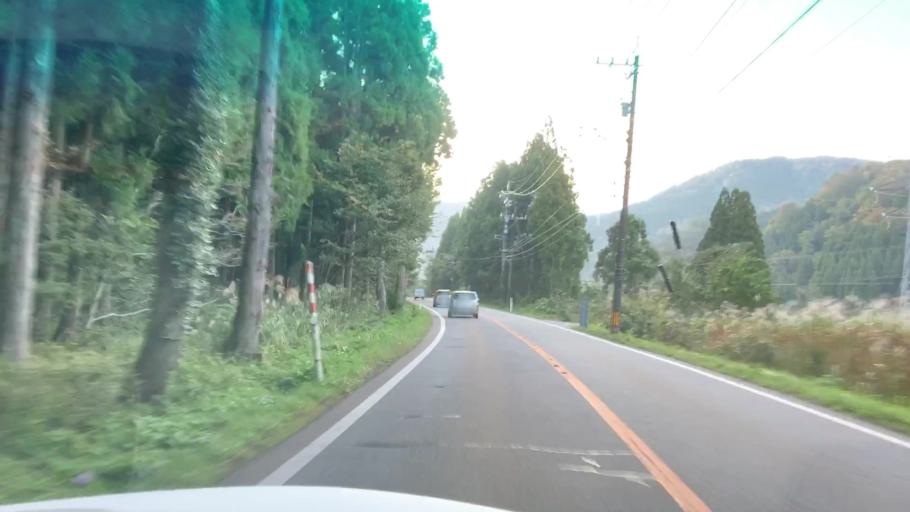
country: JP
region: Toyama
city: Kamiichi
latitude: 36.5775
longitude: 137.3417
